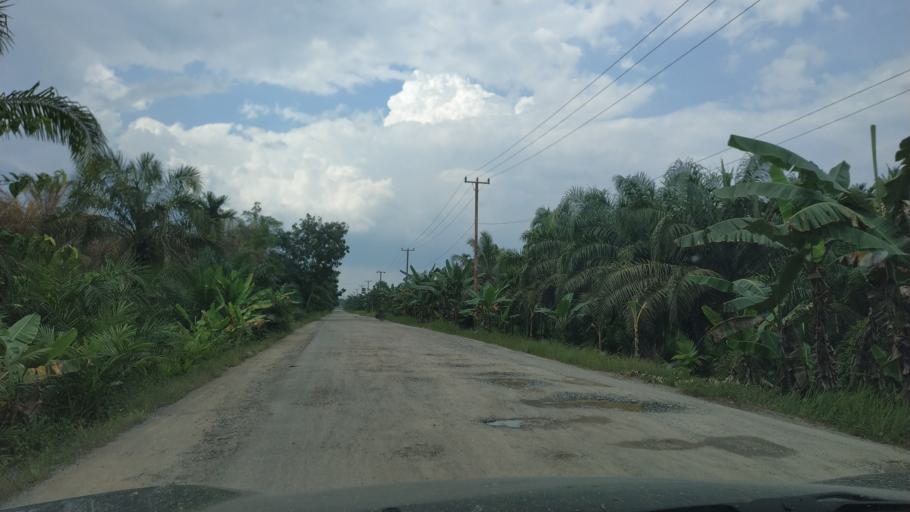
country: ID
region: Riau
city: Sungaisalak
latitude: -0.5253
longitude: 103.0046
